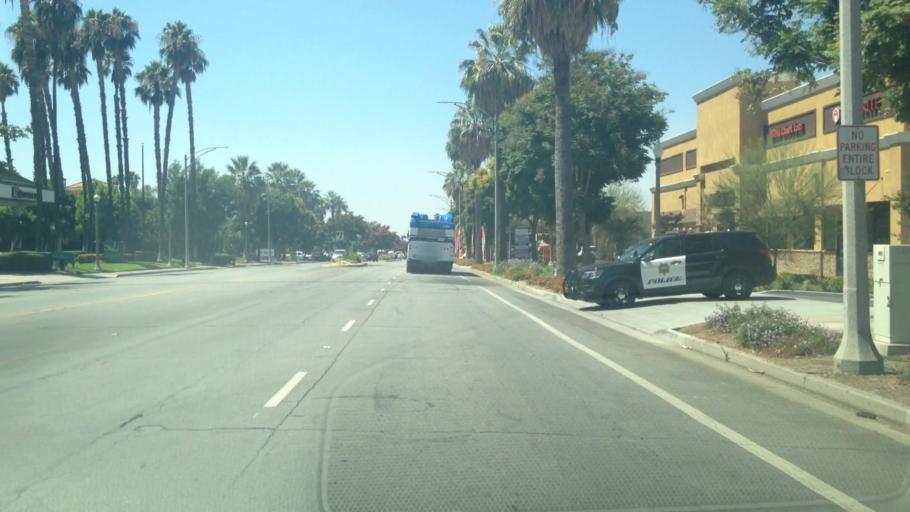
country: US
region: California
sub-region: Riverside County
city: Highgrove
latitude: 33.9757
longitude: -117.3453
